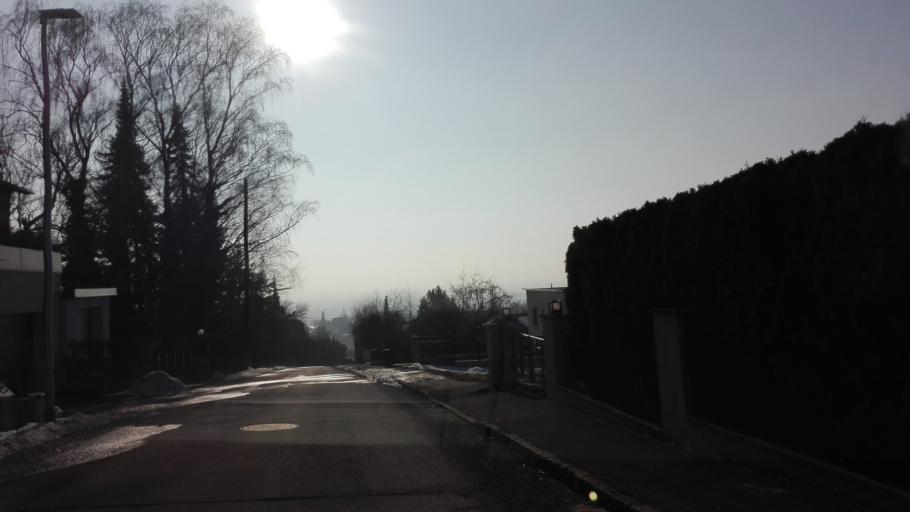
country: AT
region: Upper Austria
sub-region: Politischer Bezirk Linz-Land
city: Leonding
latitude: 48.2868
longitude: 14.2601
